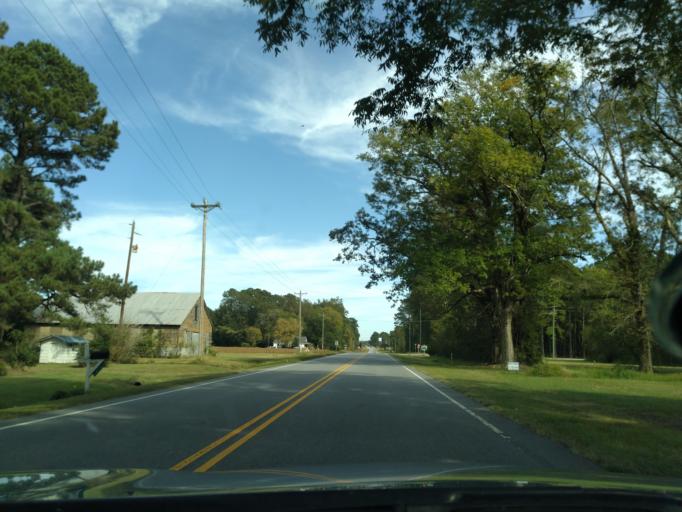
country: US
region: North Carolina
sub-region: Beaufort County
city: River Road
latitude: 35.5219
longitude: -76.8147
